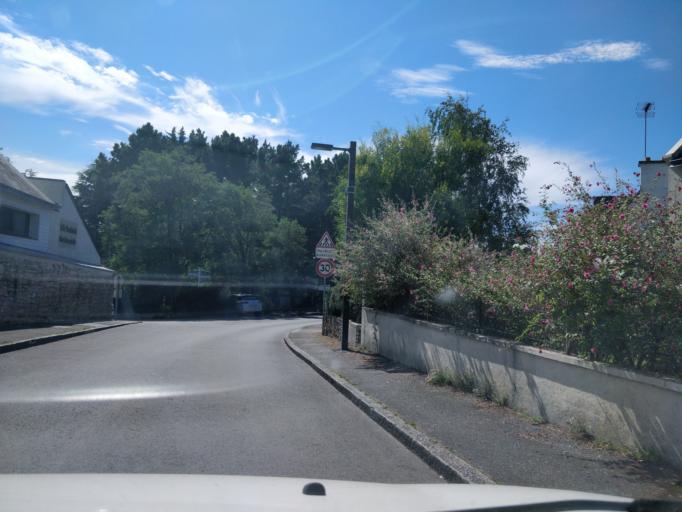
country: FR
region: Brittany
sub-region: Departement du Morbihan
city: Saint-Philibert
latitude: 47.5850
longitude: -2.9994
